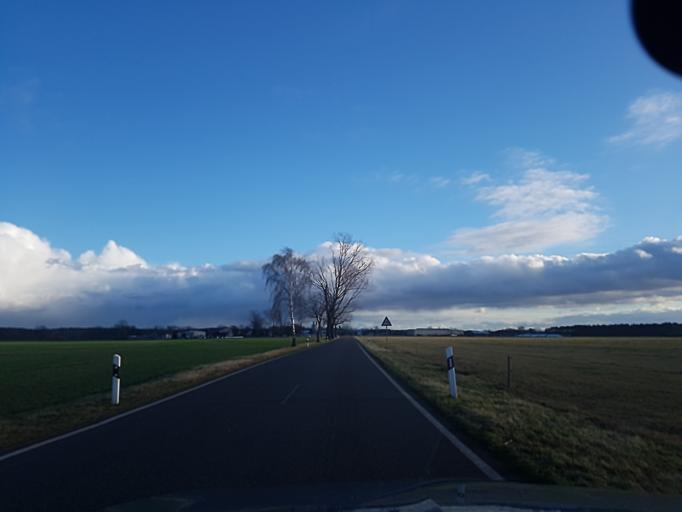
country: DE
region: Brandenburg
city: Schilda
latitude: 51.5571
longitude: 13.3517
